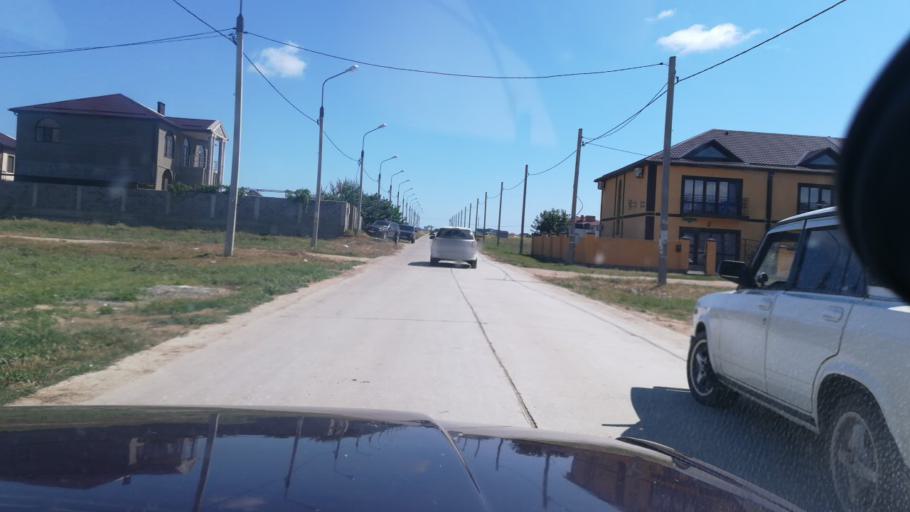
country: RU
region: Krasnodarskiy
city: Vityazevo
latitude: 44.9912
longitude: 37.2755
